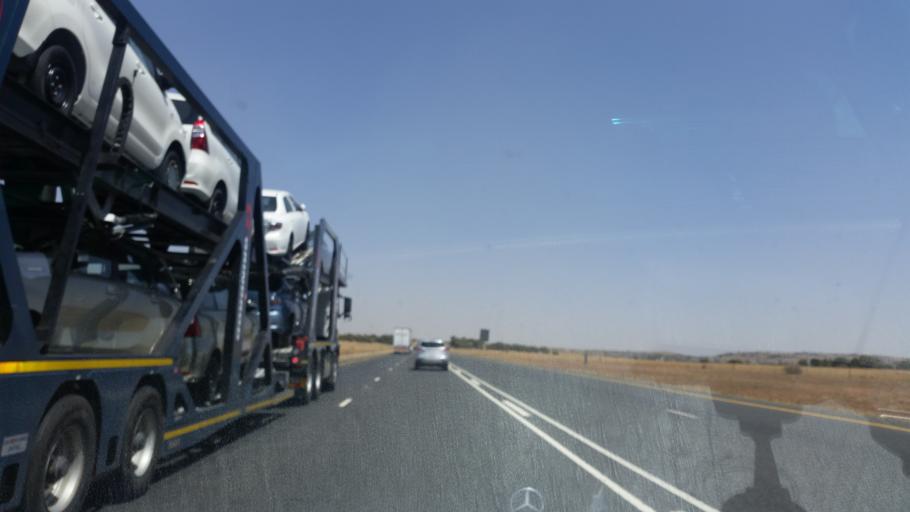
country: ZA
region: Orange Free State
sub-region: Lejweleputswa District Municipality
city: Winburg
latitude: -28.6925
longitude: 26.8120
